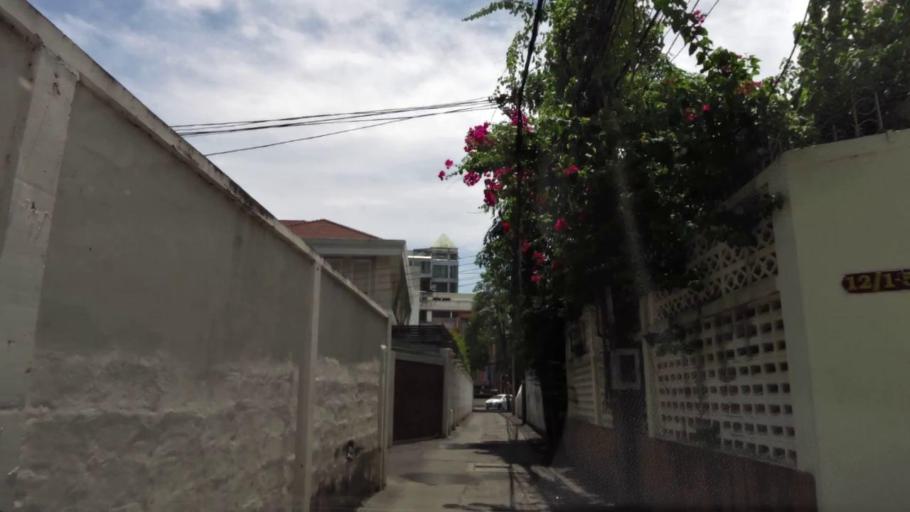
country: TH
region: Bangkok
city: Khlong Toei
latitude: 13.7365
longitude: 100.5646
